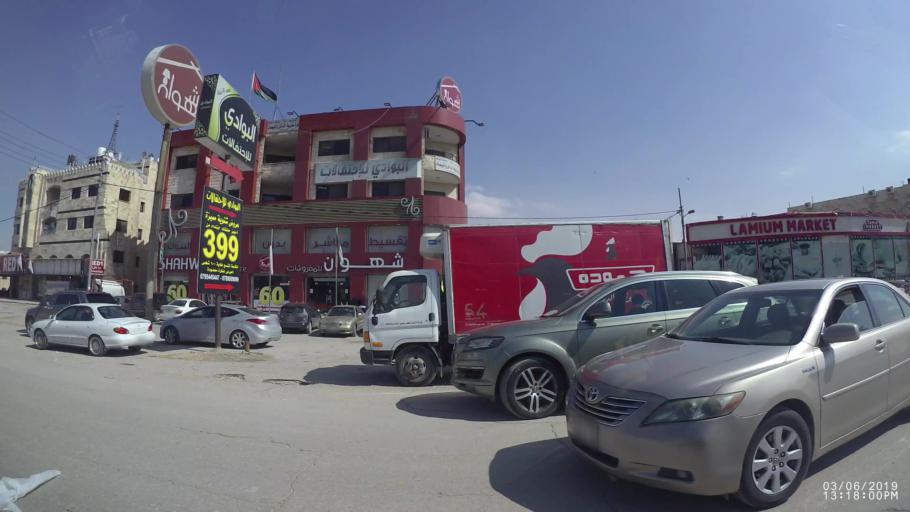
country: JO
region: Zarqa
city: Zarqa
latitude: 32.0334
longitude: 36.0903
